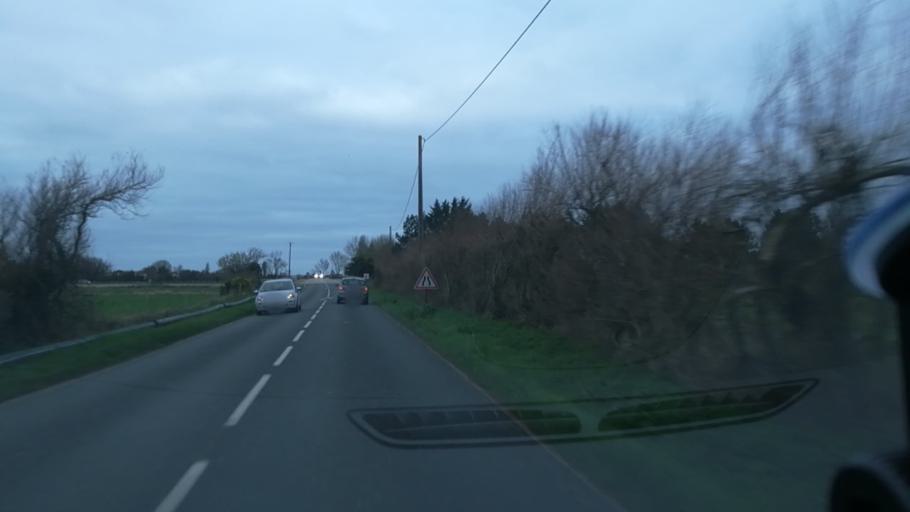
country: FR
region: Lower Normandy
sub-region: Departement de la Manche
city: Reville
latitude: 49.6107
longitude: -1.2566
